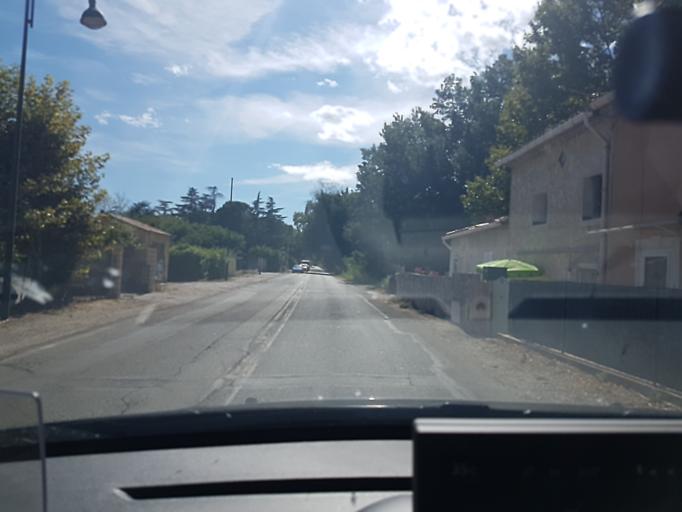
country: FR
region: Provence-Alpes-Cote d'Azur
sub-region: Departement du Vaucluse
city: Caumont-sur-Durance
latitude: 43.8923
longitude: 4.9353
